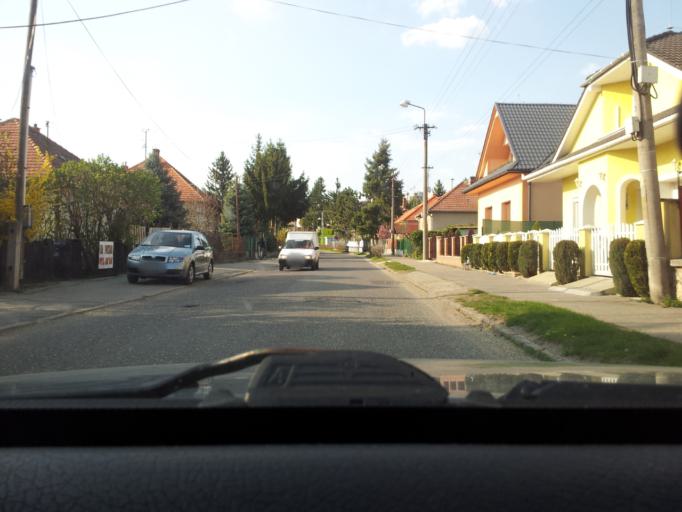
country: SK
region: Nitriansky
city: Levice
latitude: 48.2171
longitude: 18.6190
